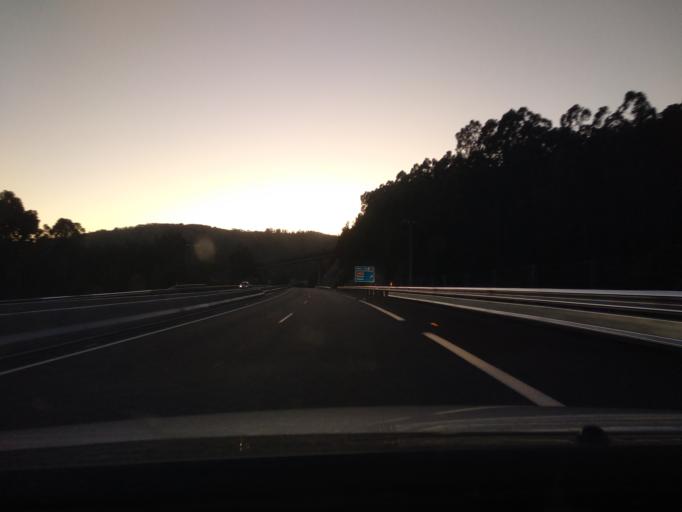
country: ES
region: Galicia
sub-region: Provincia de Pontevedra
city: Moana
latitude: 42.3092
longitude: -8.7272
